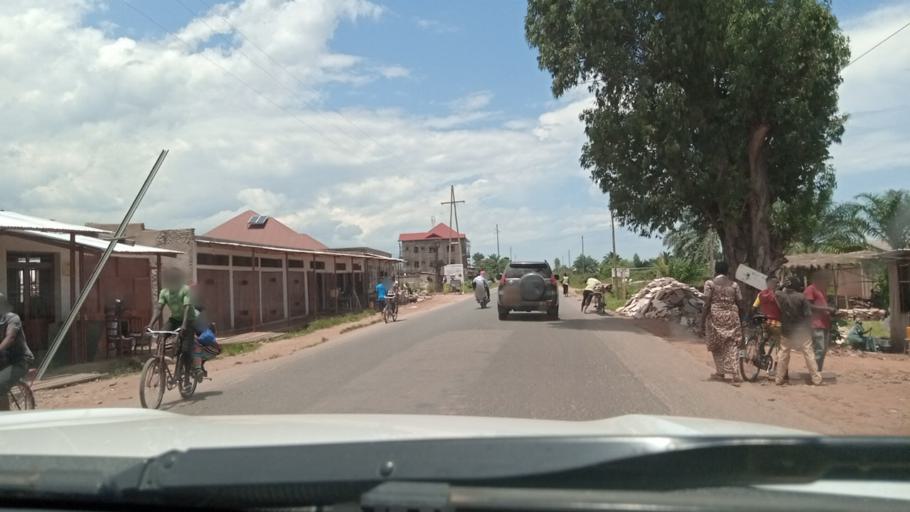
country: BI
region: Bujumbura Mairie
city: Bujumbura
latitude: -3.4622
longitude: 29.3505
